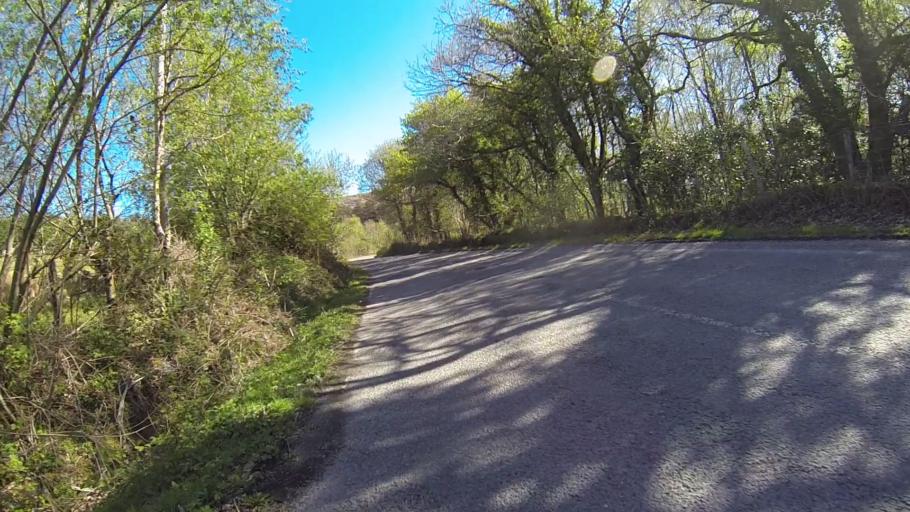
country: IE
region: Munster
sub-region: Ciarrai
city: Kenmare
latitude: 51.7699
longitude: -9.7551
